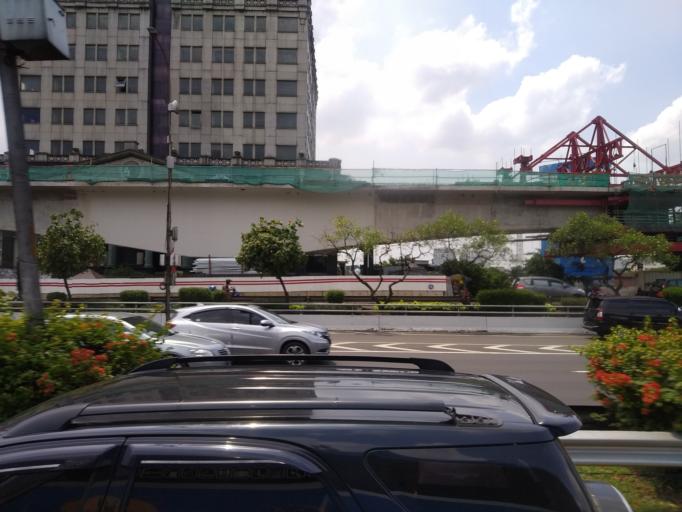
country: ID
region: Jakarta Raya
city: Jakarta
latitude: -6.2433
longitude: 106.8590
